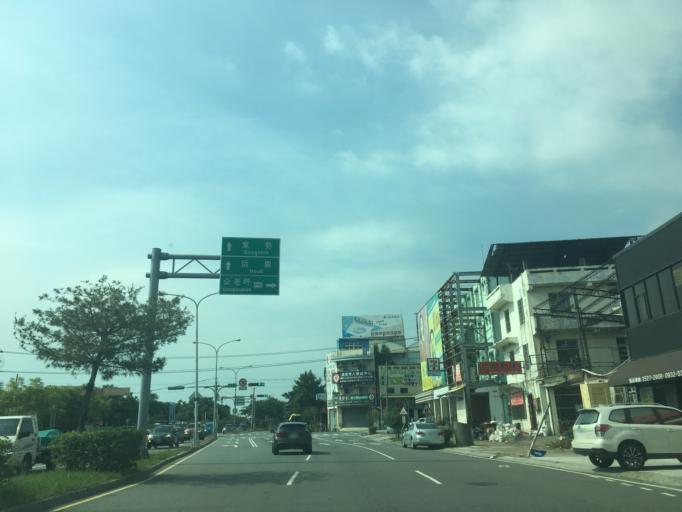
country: TW
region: Taiwan
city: Fengyuan
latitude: 24.2549
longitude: 120.7374
